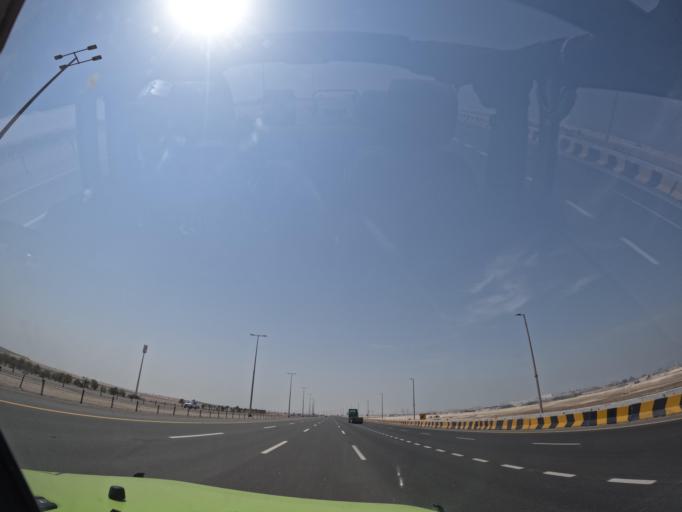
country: AE
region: Abu Dhabi
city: Abu Dhabi
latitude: 24.2720
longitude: 54.5059
